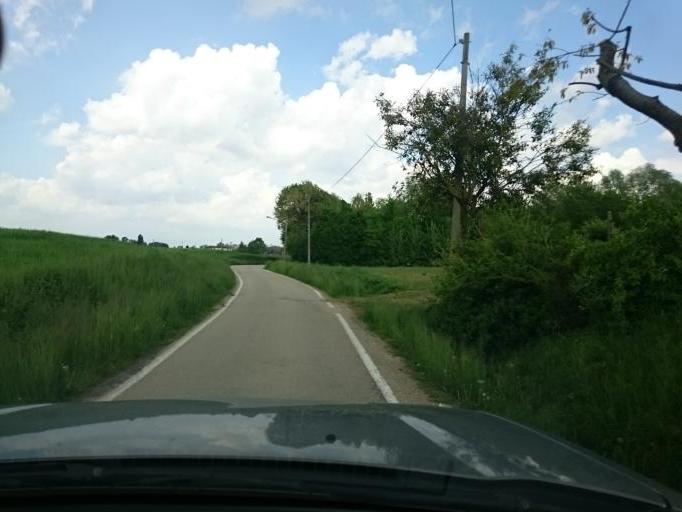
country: IT
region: Veneto
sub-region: Provincia di Vicenza
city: Torri di Quartesolo
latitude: 45.5197
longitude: 11.5853
